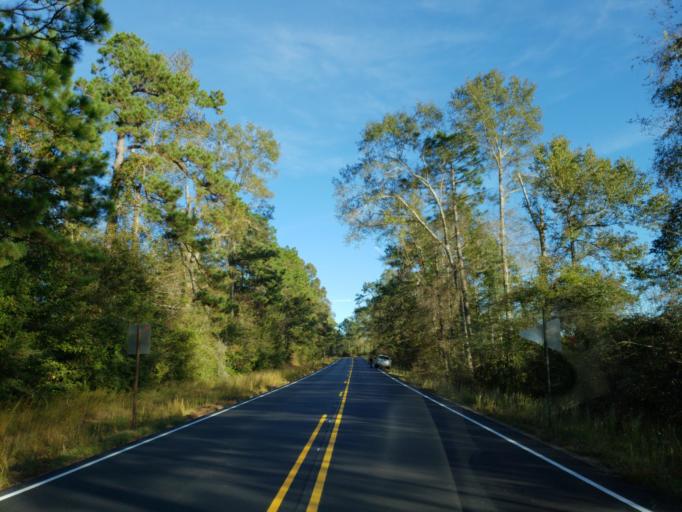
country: US
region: Mississippi
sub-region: Perry County
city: Richton
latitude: 31.3478
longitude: -88.7775
